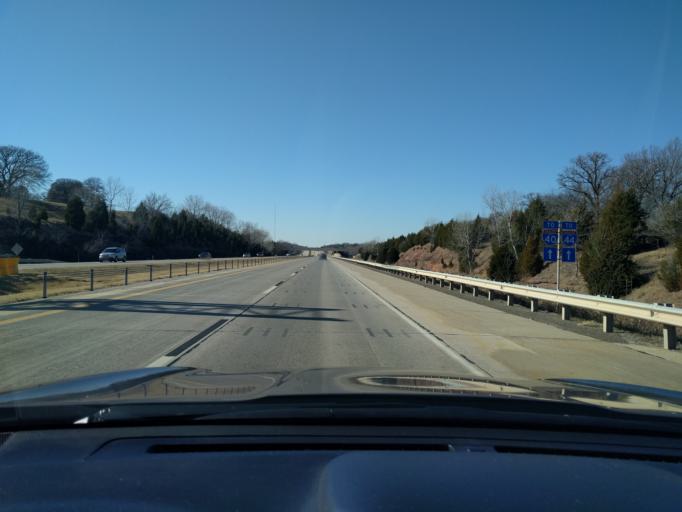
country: US
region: Oklahoma
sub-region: Oklahoma County
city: Edmond
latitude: 35.6013
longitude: -97.4373
